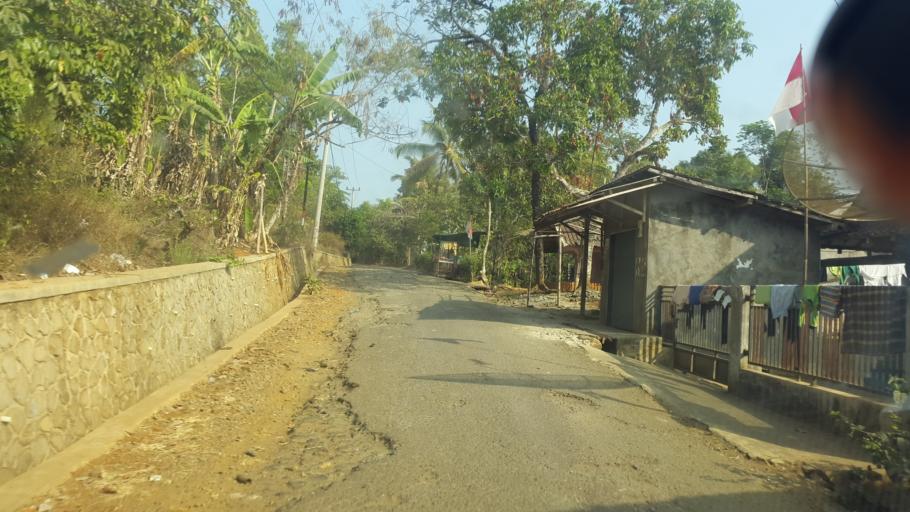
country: ID
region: West Java
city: Jampang Kulon
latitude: -7.2574
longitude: 106.6201
